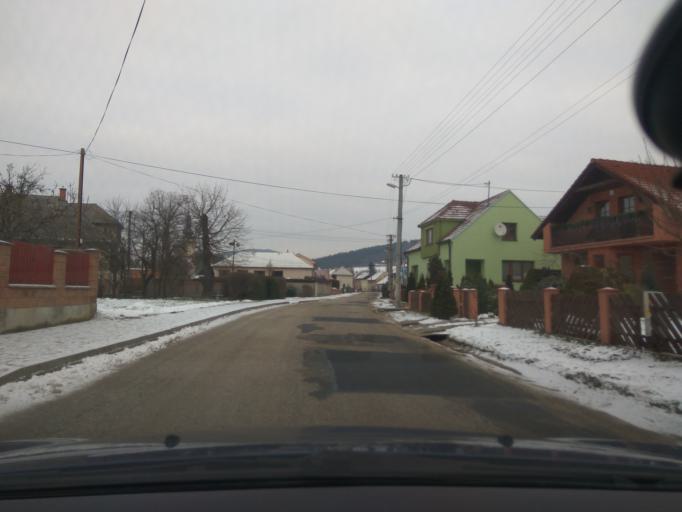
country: SK
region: Nitriansky
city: Stara Tura
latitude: 48.7857
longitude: 17.7349
